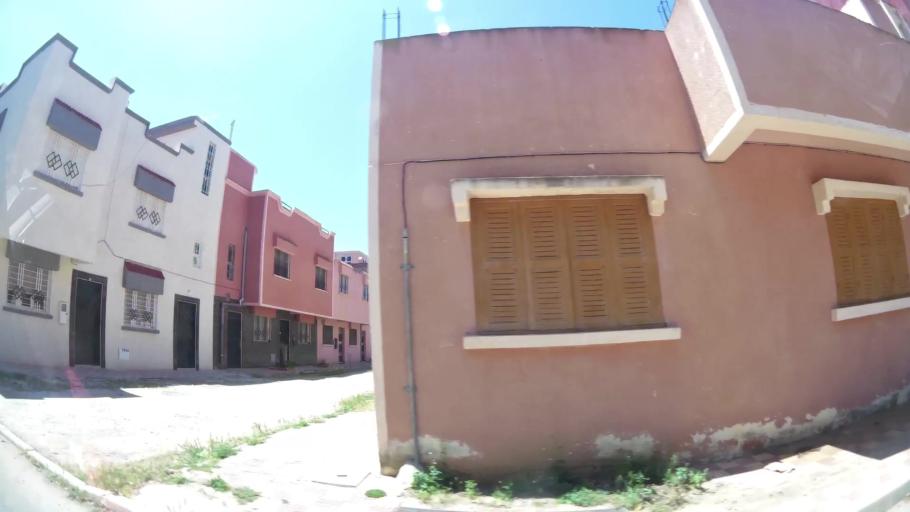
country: MA
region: Oriental
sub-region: Berkane-Taourirt
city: Madagh
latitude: 35.0755
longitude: -2.2185
